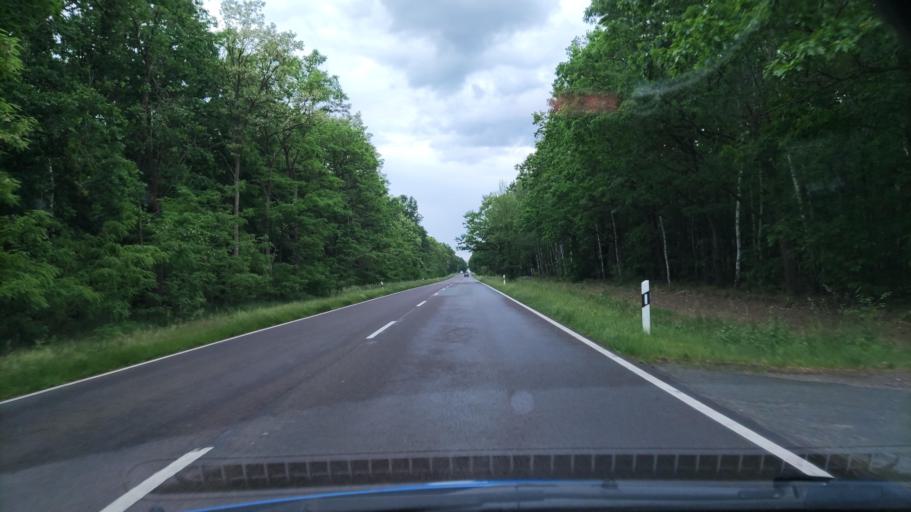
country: DE
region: Saxony-Anhalt
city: Letzlingen
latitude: 52.3991
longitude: 11.4732
